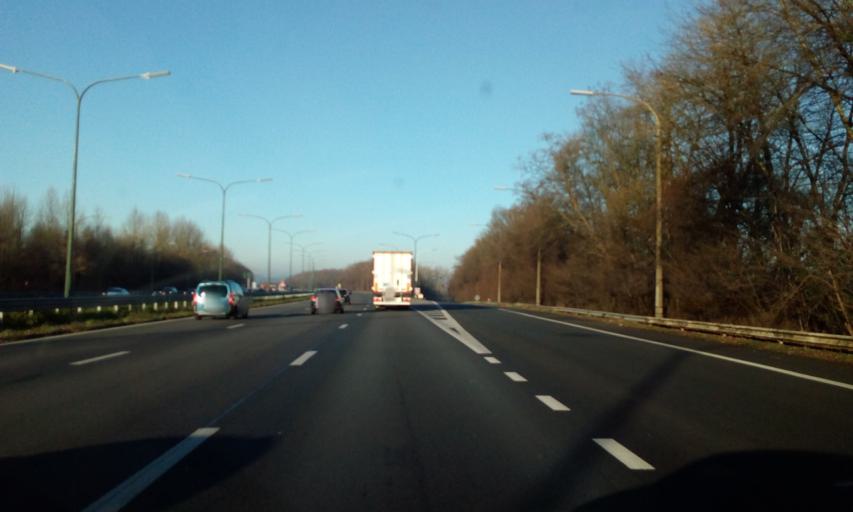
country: BE
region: Wallonia
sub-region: Province du Brabant Wallon
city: Nivelles
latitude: 50.5813
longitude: 4.3060
